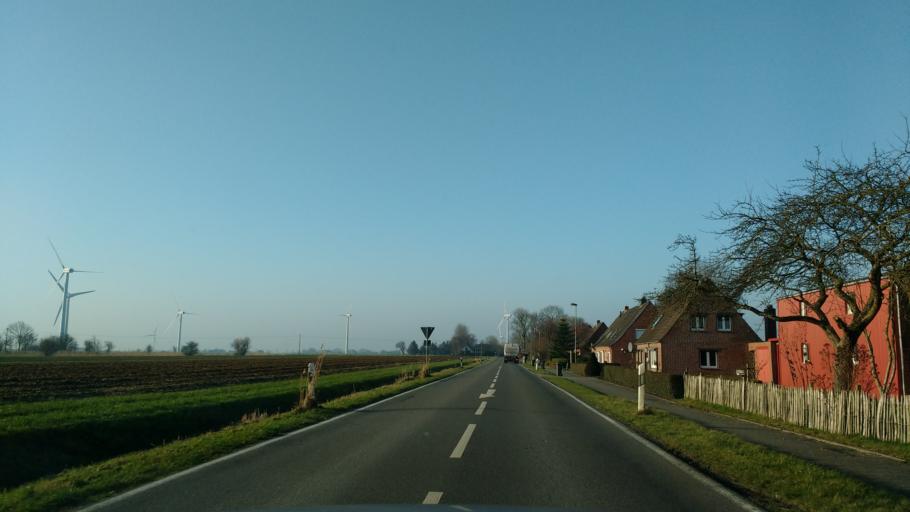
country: DE
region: Schleswig-Holstein
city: Trennewurth
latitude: 54.0004
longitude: 9.0240
